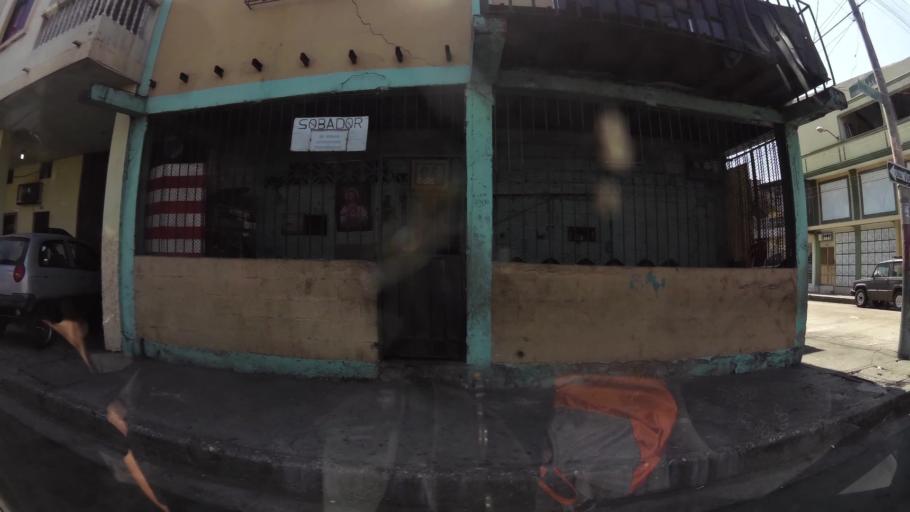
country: EC
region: Guayas
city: Guayaquil
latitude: -2.1958
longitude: -79.9134
